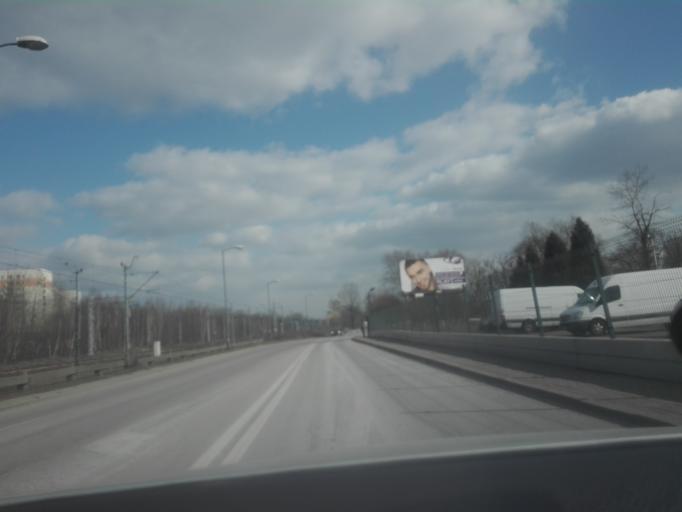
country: PL
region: Silesian Voivodeship
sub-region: Katowice
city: Katowice
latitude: 50.2630
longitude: 18.9918
